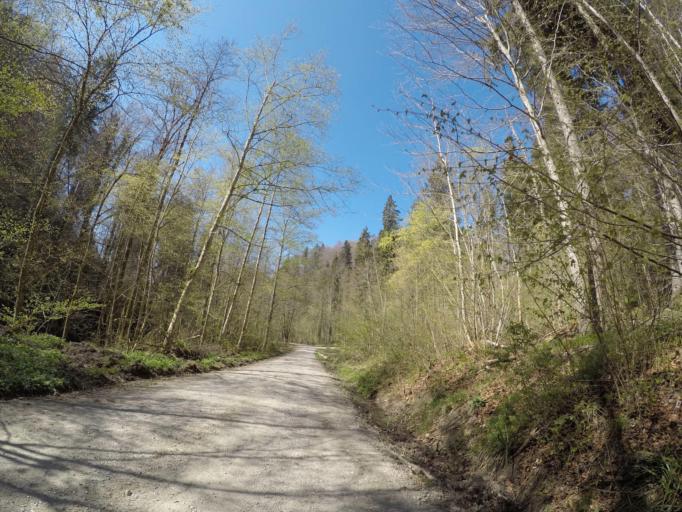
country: DE
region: Baden-Wuerttemberg
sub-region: Tuebingen Region
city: Horgenzell
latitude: 47.8021
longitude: 9.4628
